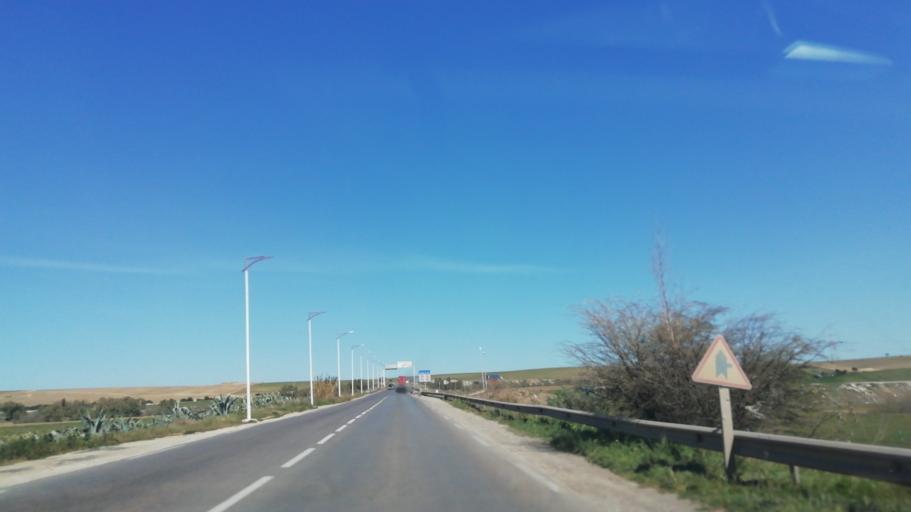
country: DZ
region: Oran
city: Sidi ech Chahmi
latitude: 35.5691
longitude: -0.5588
